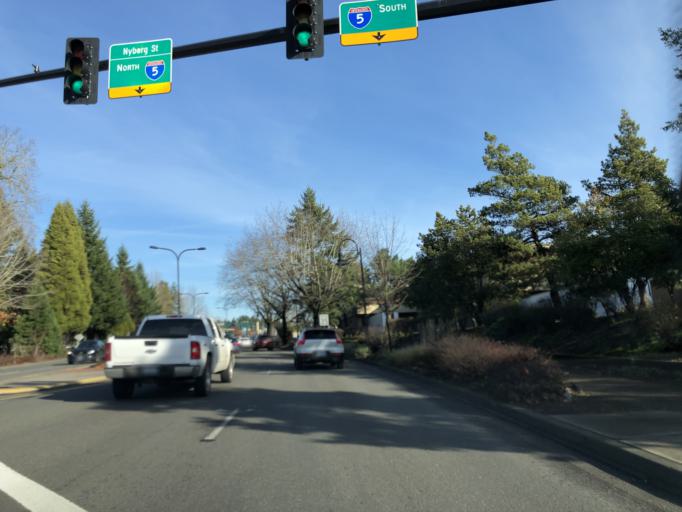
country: US
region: Oregon
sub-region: Washington County
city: Tualatin
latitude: 45.3814
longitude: -122.7591
